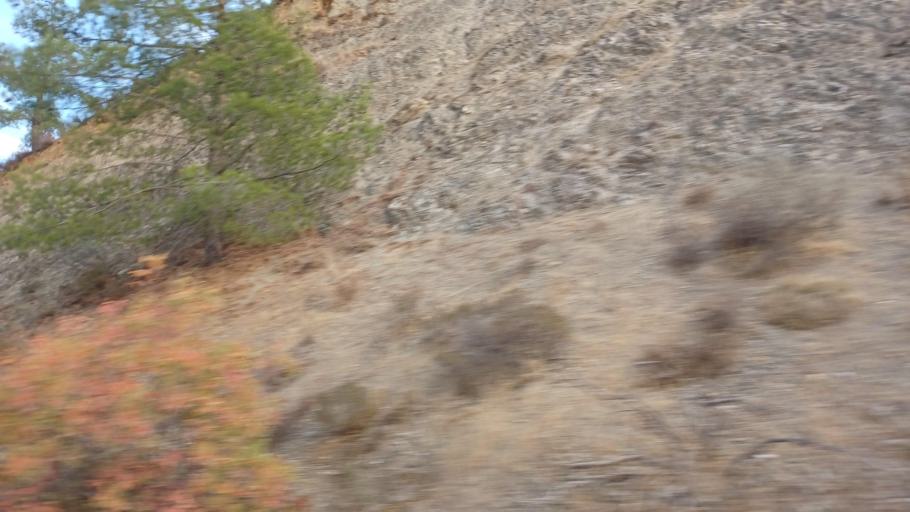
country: CY
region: Lefkosia
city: Kakopetria
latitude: 34.9874
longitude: 32.9063
